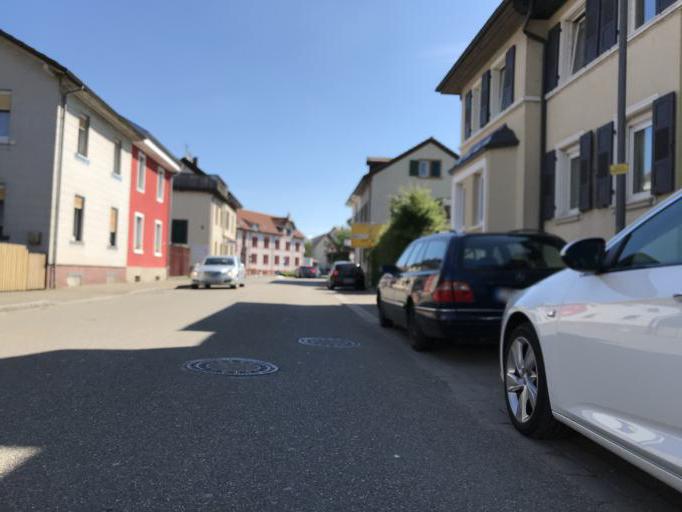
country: DE
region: Baden-Wuerttemberg
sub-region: Freiburg Region
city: Schopfheim
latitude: 47.6486
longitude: 7.8271
